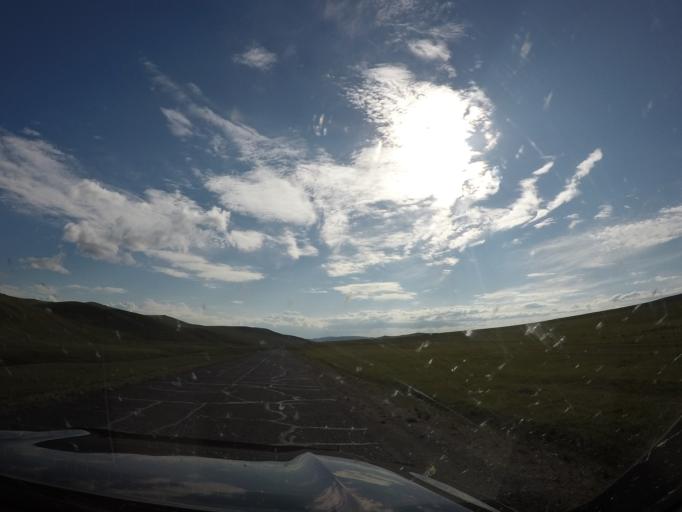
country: MN
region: Hentiy
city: Modot
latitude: 47.8020
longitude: 108.7012
